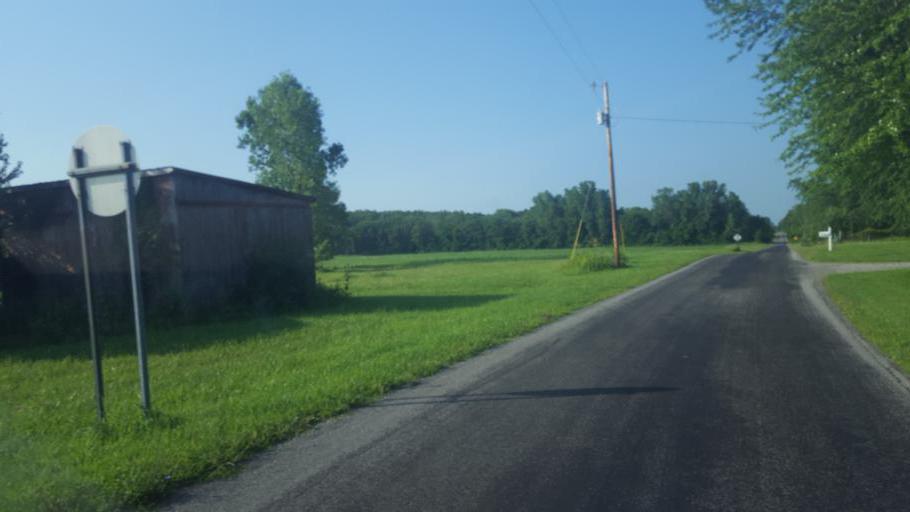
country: US
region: Ohio
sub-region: Hardin County
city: Kenton
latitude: 40.5747
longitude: -83.5756
